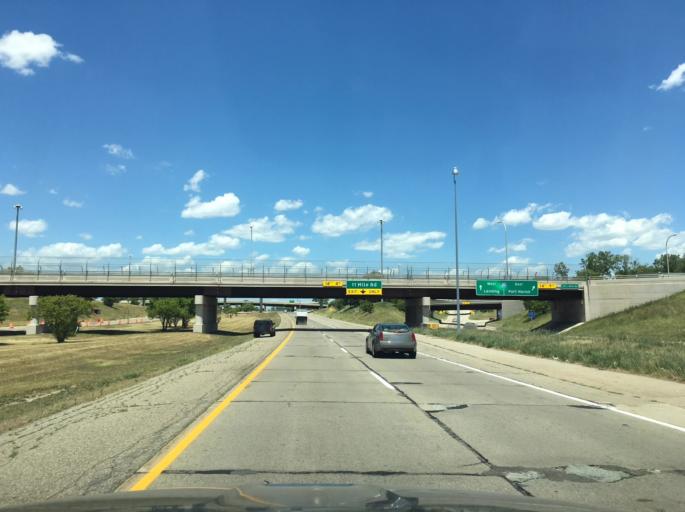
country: US
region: Michigan
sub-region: Macomb County
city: Center Line
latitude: 42.4835
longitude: -83.0454
